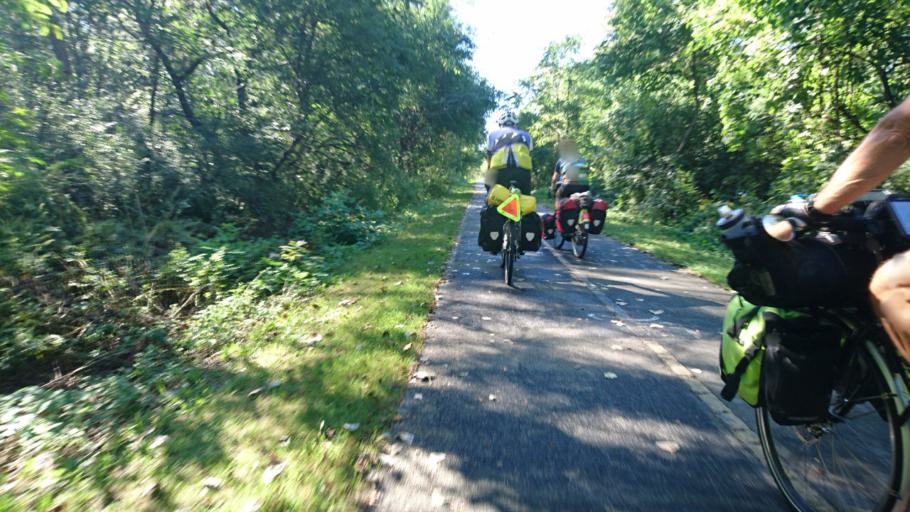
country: US
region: Indiana
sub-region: Lake County
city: Whiting
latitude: 41.6870
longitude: -87.5304
